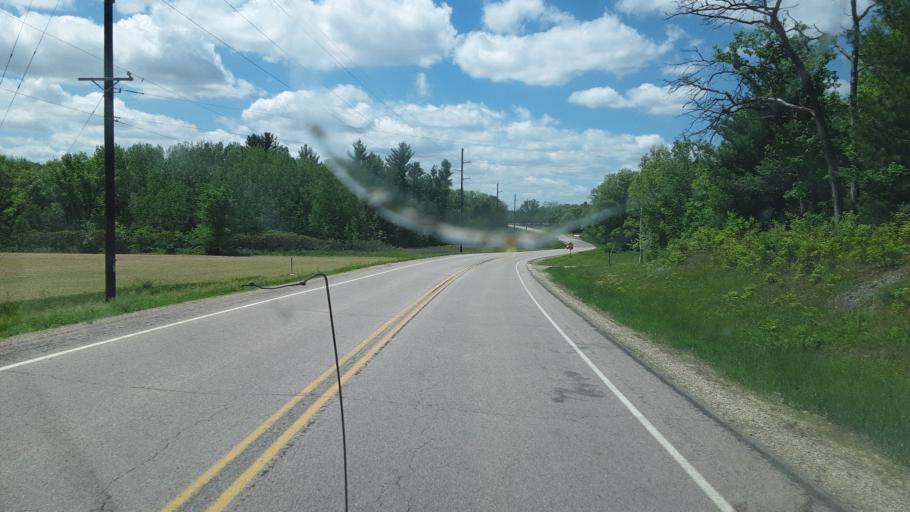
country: US
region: Wisconsin
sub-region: Sauk County
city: Lake Delton
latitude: 43.5902
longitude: -89.8948
